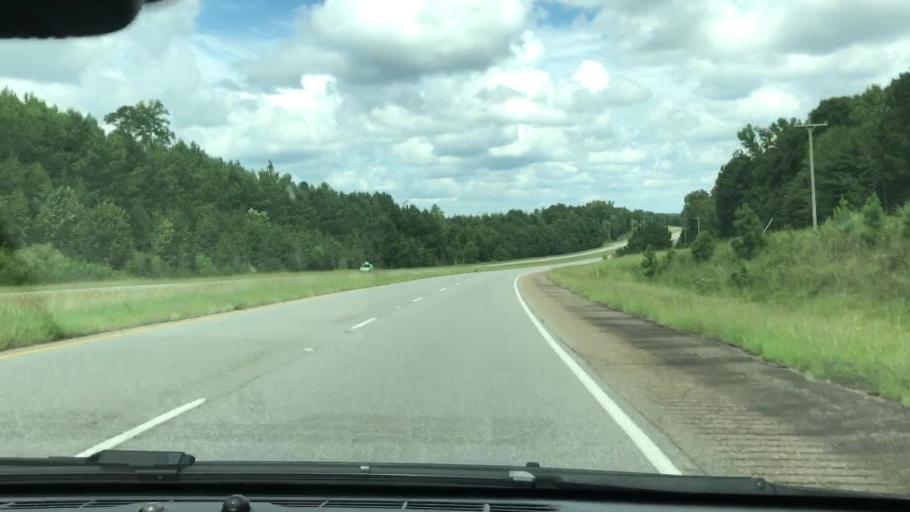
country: US
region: Georgia
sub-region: Stewart County
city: Lumpkin
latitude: 32.1247
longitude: -84.8217
